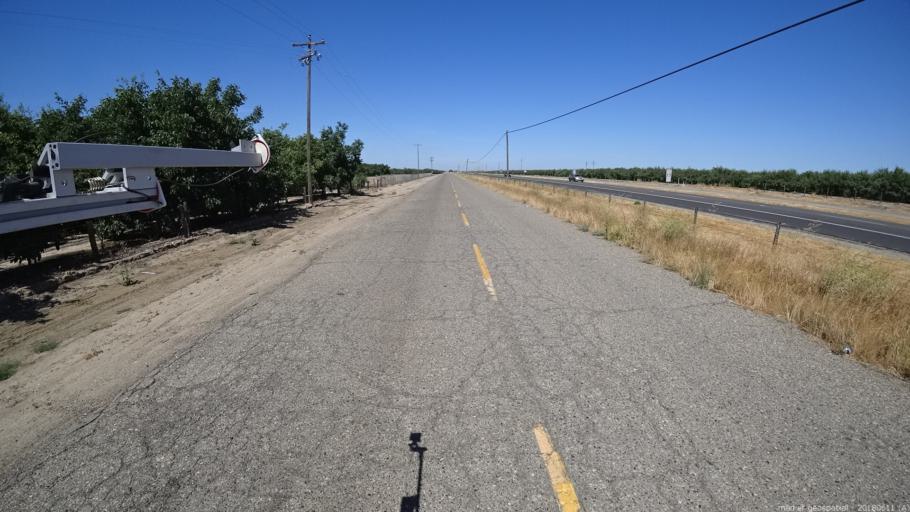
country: US
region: California
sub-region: Madera County
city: Fairmead
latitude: 37.0836
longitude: -120.2175
